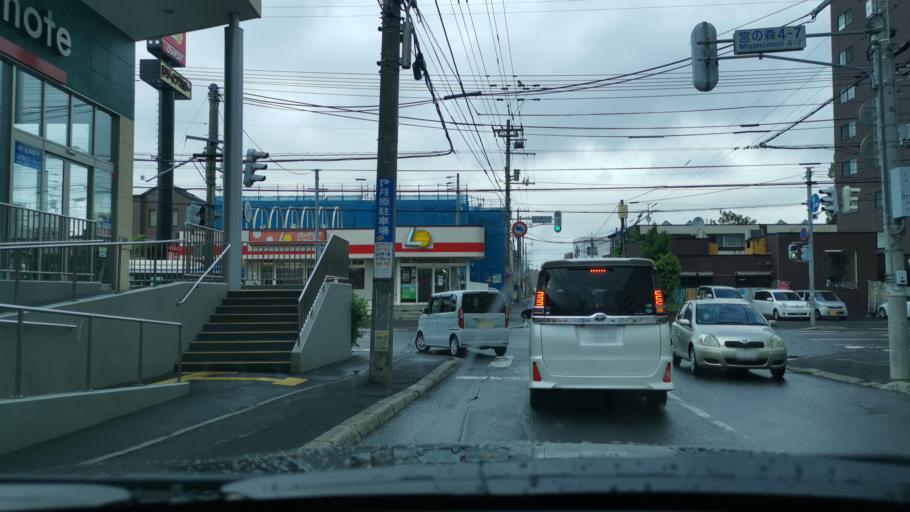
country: JP
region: Hokkaido
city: Sapporo
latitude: 43.0642
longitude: 141.3004
